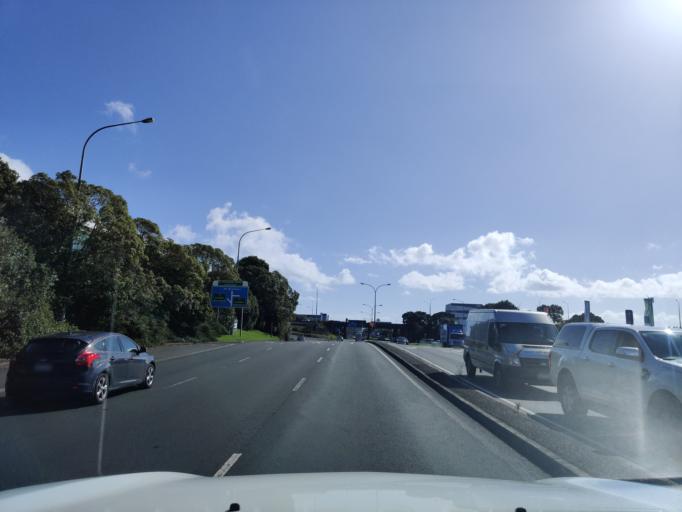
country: NZ
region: Auckland
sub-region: Auckland
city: Tamaki
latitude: -36.9211
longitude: 174.8405
